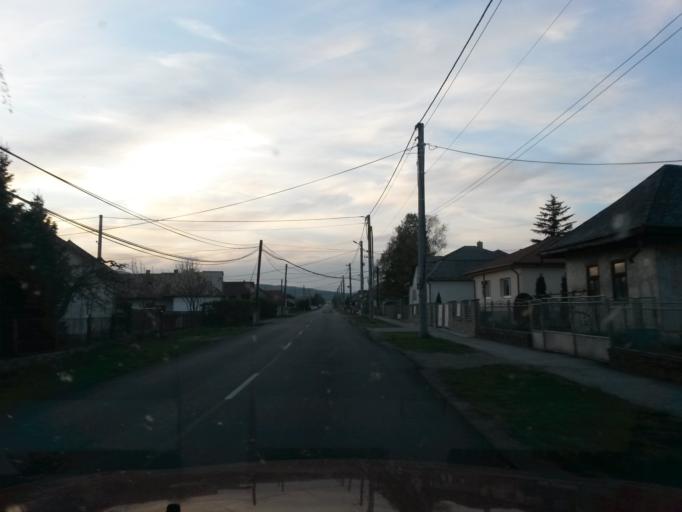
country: HU
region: Borsod-Abauj-Zemplen
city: Satoraljaujhely
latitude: 48.5295
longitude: 21.5816
